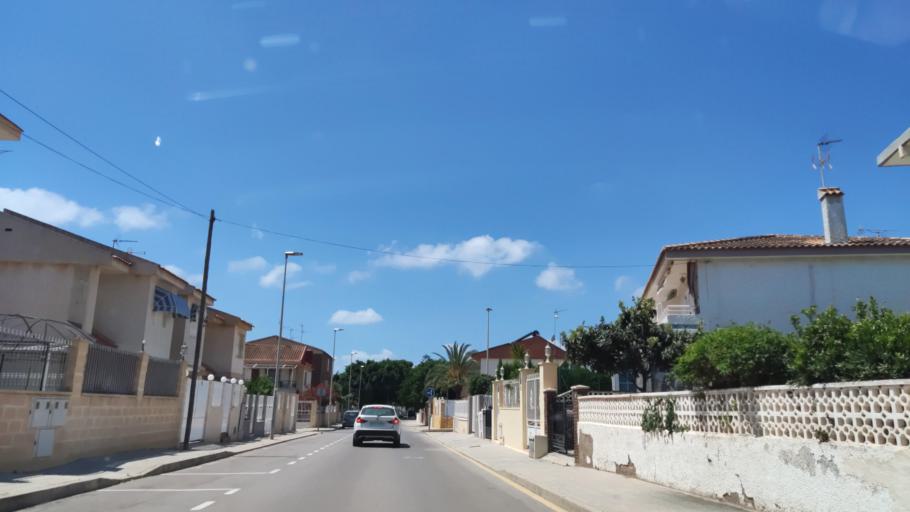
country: ES
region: Murcia
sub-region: Murcia
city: Los Alcazares
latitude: 37.7571
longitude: -0.8367
